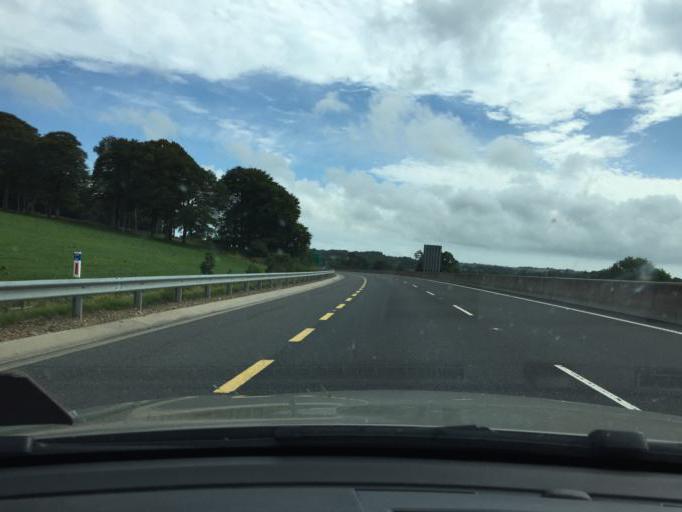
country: IE
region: Leinster
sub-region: Kilkenny
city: Mooncoin
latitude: 52.2489
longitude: -7.1909
